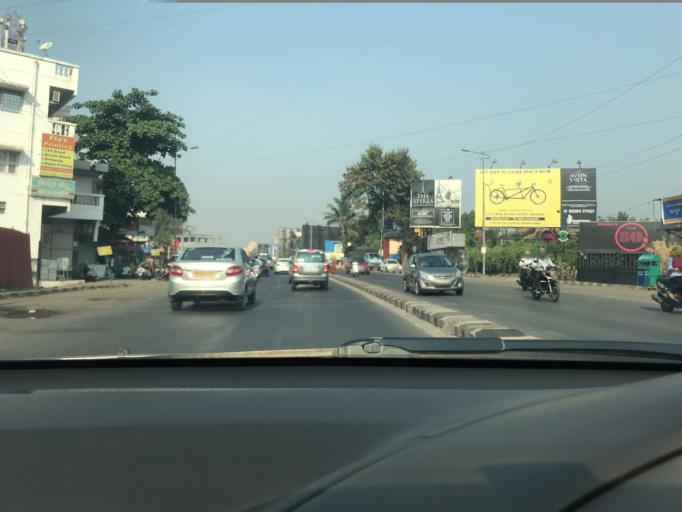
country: IN
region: Maharashtra
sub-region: Pune Division
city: Khadki
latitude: 18.5543
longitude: 73.8016
